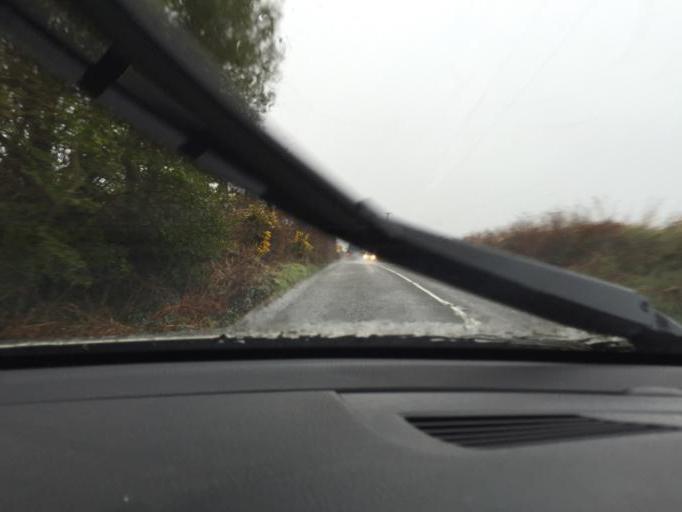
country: IE
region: Munster
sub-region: Ciarrai
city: Dingle
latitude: 52.1372
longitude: -10.2999
